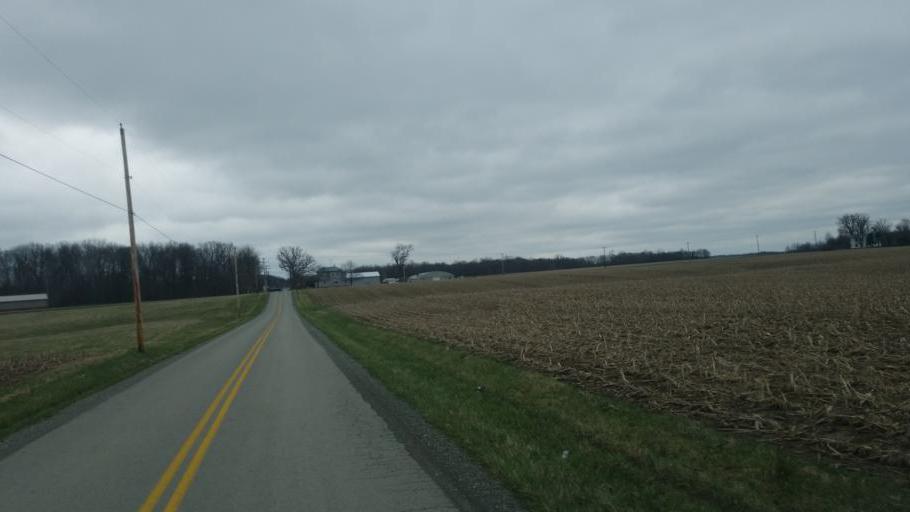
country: US
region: Ohio
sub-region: Wyandot County
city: Upper Sandusky
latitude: 40.7890
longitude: -83.2783
